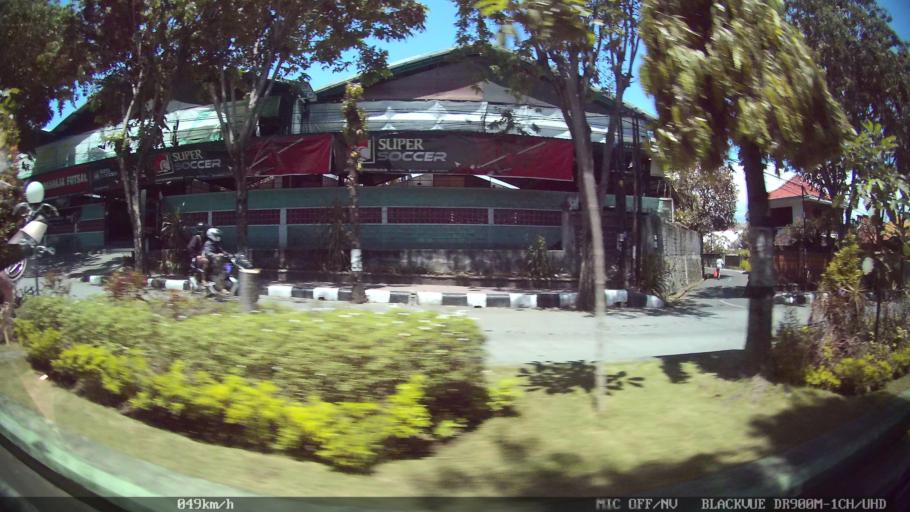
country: ID
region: Bali
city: Singaraja
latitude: -8.1152
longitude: 115.0904
